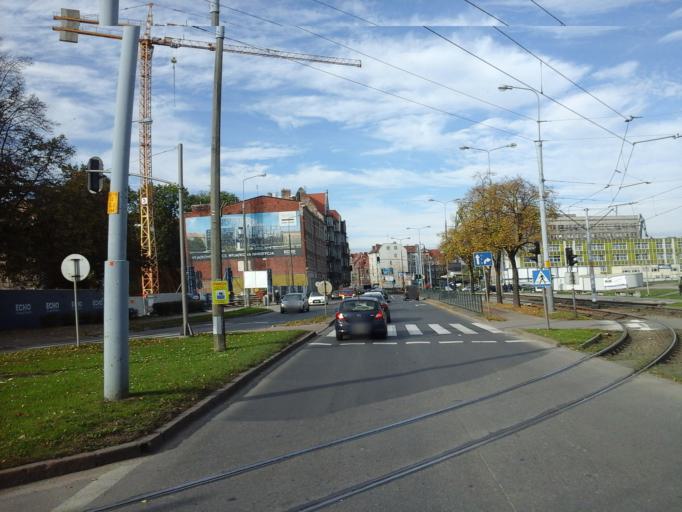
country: PL
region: Pomeranian Voivodeship
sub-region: Gdansk
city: Gdansk
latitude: 54.3597
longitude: 18.6484
